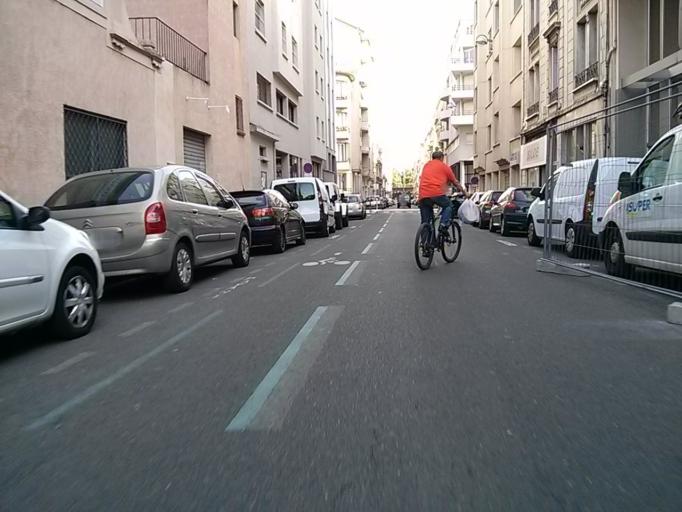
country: FR
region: Rhone-Alpes
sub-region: Departement de la Loire
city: Saint-Etienne
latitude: 45.4437
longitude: 4.3866
